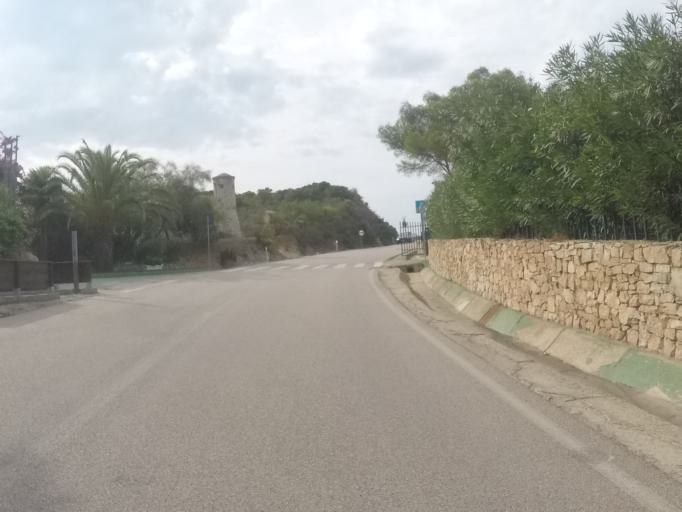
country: IT
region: Sardinia
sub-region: Provincia di Olbia-Tempio
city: Palau
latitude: 41.1752
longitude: 9.3996
